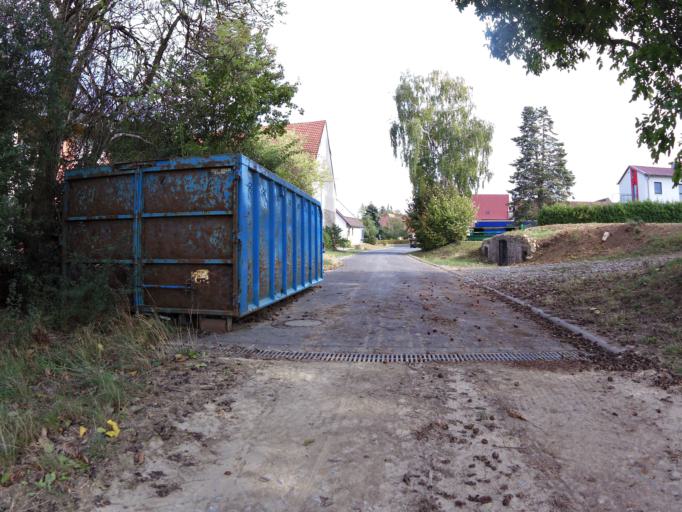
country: DE
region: Bavaria
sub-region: Regierungsbezirk Unterfranken
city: Eibelstadt
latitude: 49.6996
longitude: 9.9657
